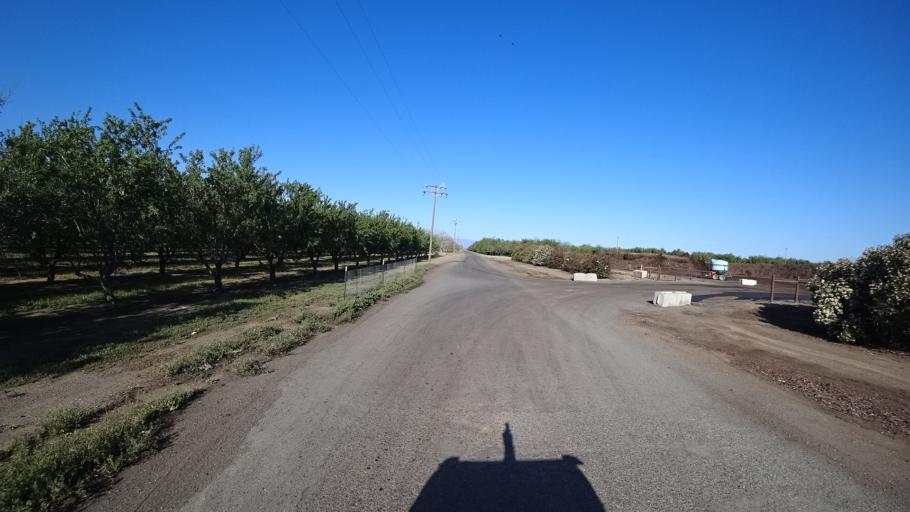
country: US
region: California
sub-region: Glenn County
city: Orland
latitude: 39.6819
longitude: -122.1579
